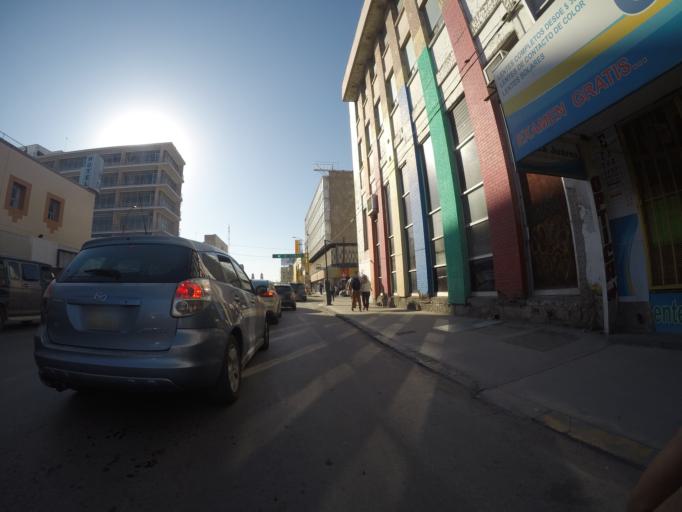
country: MX
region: Chihuahua
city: Ciudad Juarez
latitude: 31.7391
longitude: -106.4812
